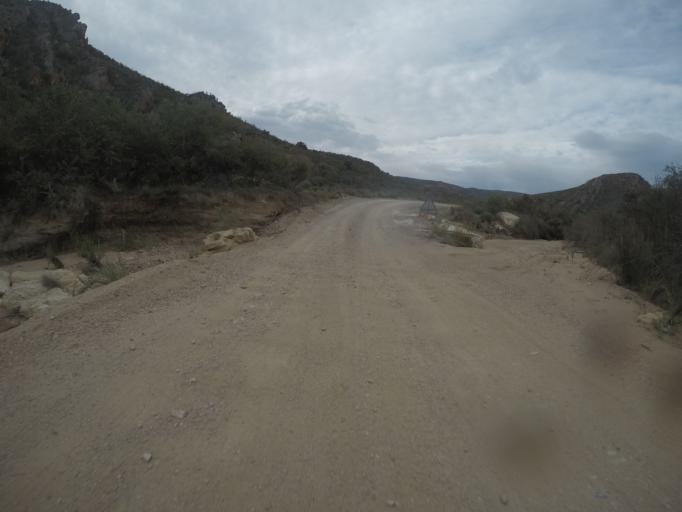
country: ZA
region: Eastern Cape
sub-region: Cacadu District Municipality
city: Willowmore
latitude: -33.5029
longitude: 23.6355
